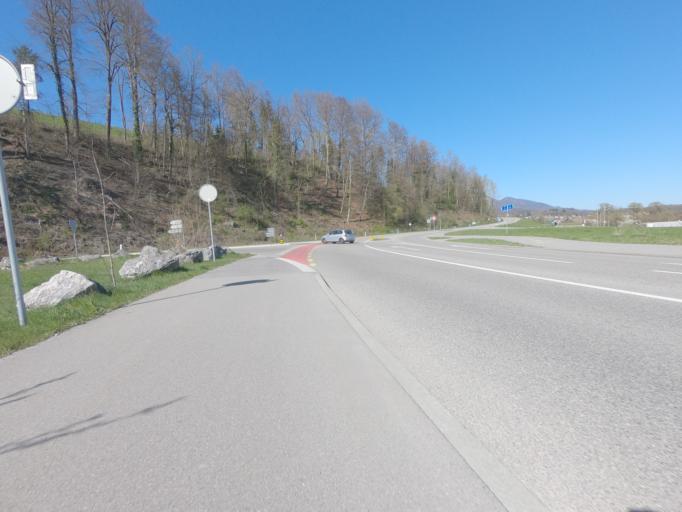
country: CH
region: Solothurn
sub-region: Bezirk Wasseramt
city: Luterbach
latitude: 47.2288
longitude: 7.5879
